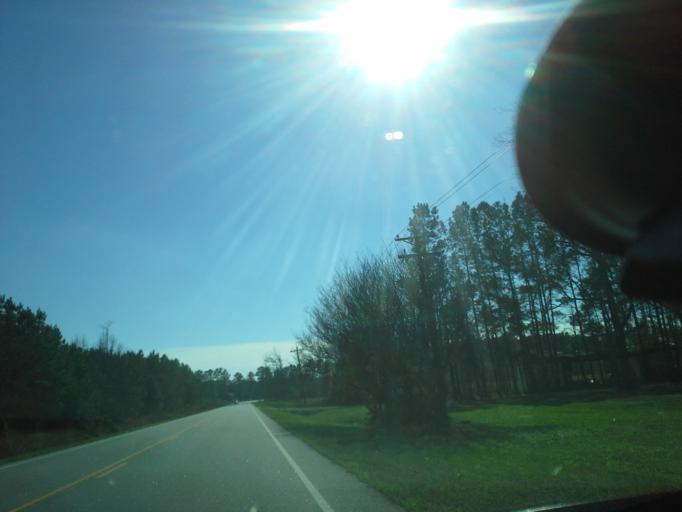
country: US
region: North Carolina
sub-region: Beaufort County
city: Belhaven
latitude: 35.5495
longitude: -76.7044
